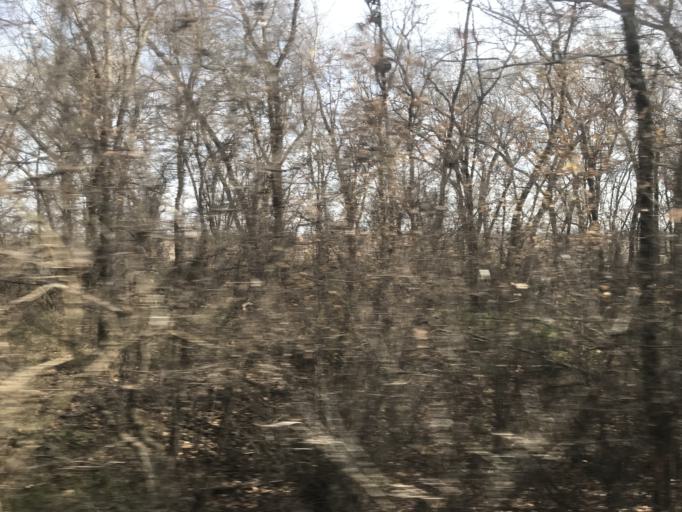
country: AR
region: Cordoba
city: Laguna Larga
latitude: -31.7400
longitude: -63.8353
